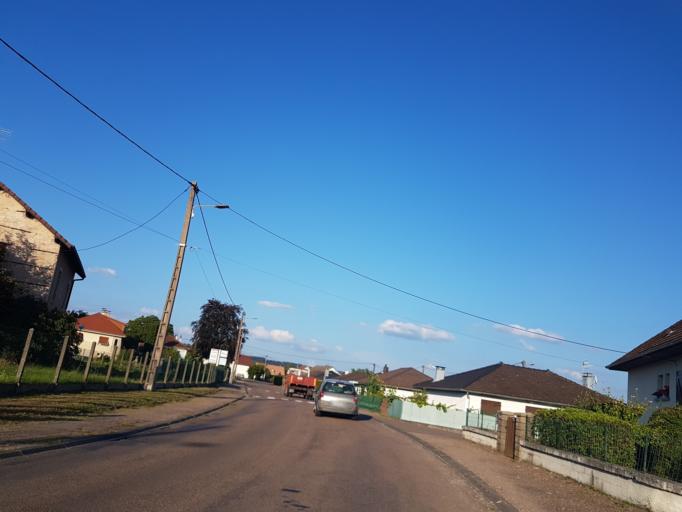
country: FR
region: Franche-Comte
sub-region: Departement de la Haute-Saone
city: Froideconche
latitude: 47.8186
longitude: 6.4070
